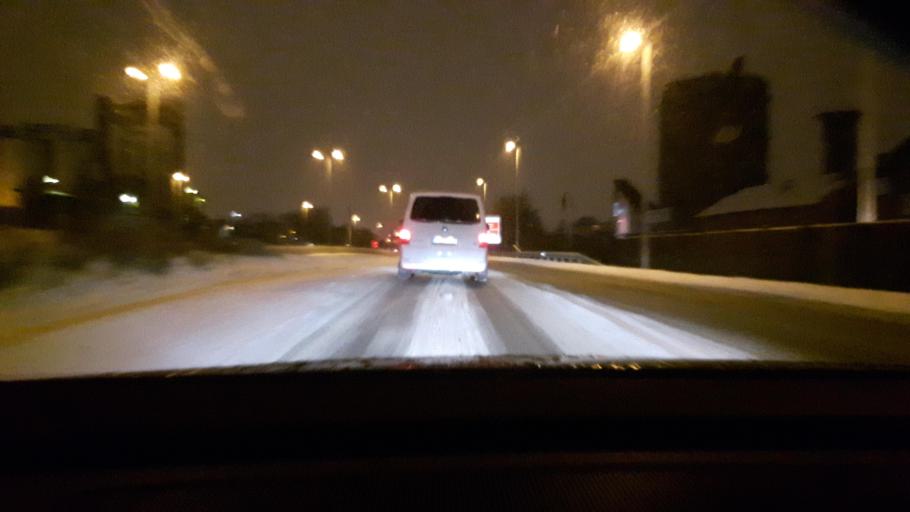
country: SE
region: Vaestra Goetaland
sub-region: Goteborg
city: Goeteborg
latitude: 57.7184
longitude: 11.9878
